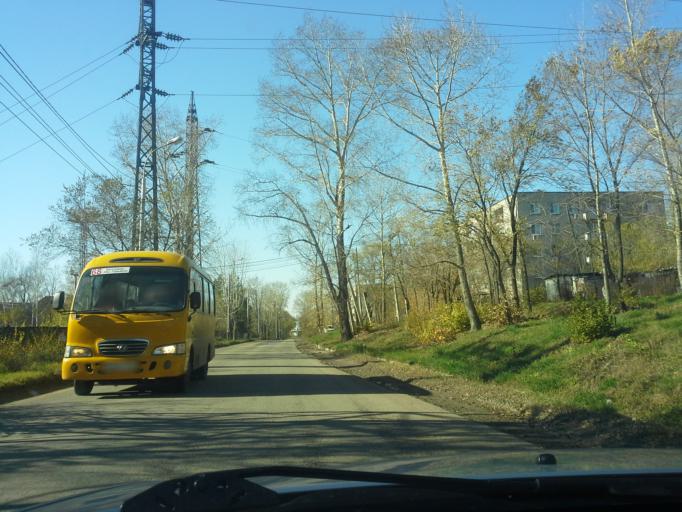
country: RU
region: Khabarovsk Krai
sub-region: Khabarovskiy Rayon
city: Khabarovsk
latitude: 48.5380
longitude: 135.0255
